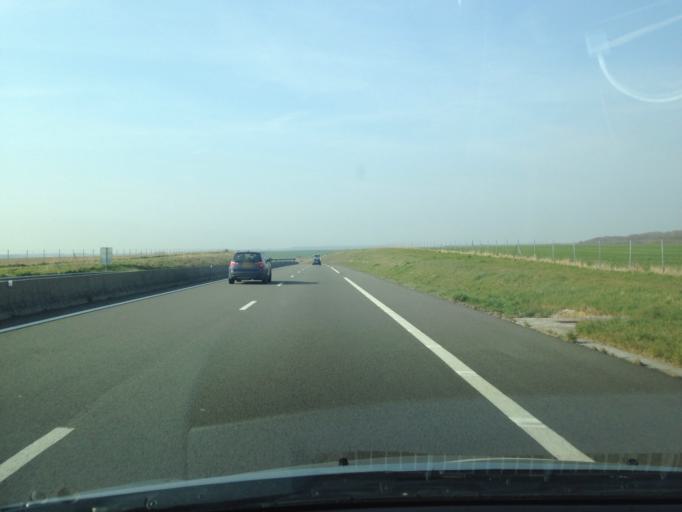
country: FR
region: Picardie
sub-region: Departement de la Somme
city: Rue
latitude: 50.3158
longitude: 1.7219
